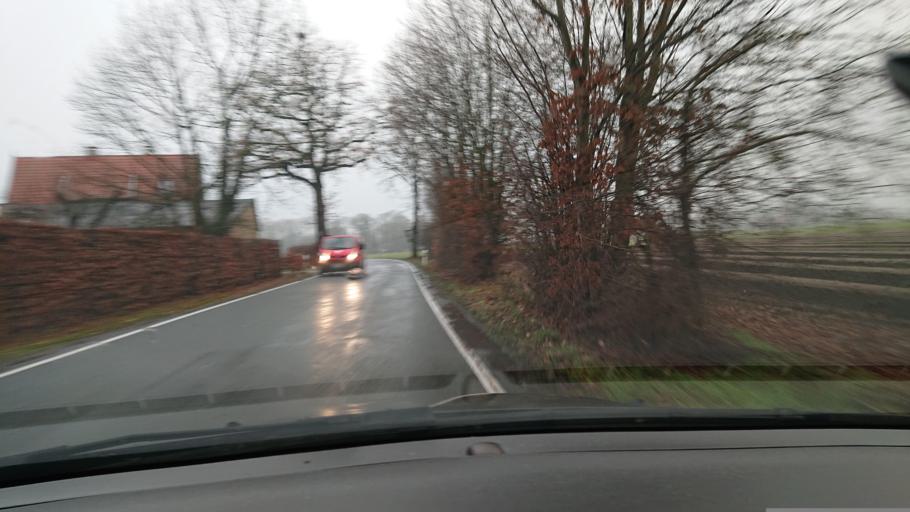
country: DE
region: North Rhine-Westphalia
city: Oelde
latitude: 51.8617
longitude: 8.2043
